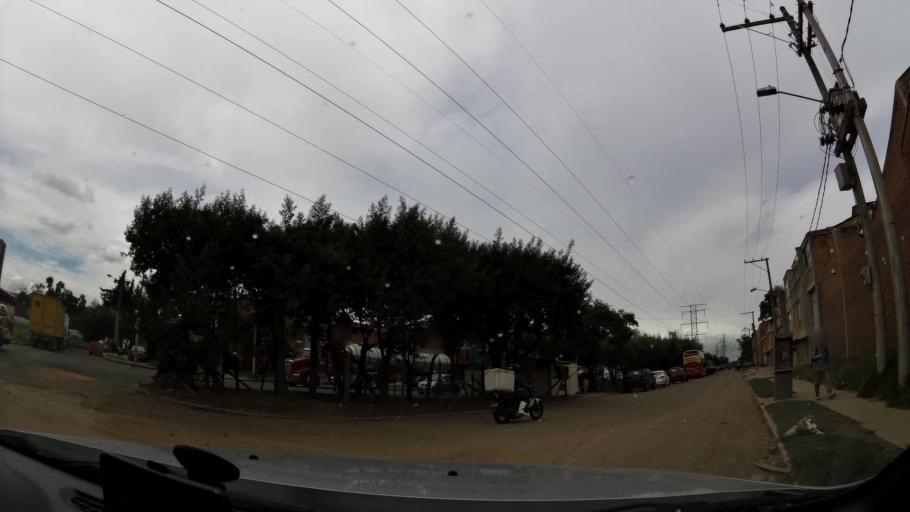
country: CO
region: Bogota D.C.
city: Bogota
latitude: 4.6358
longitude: -74.1234
